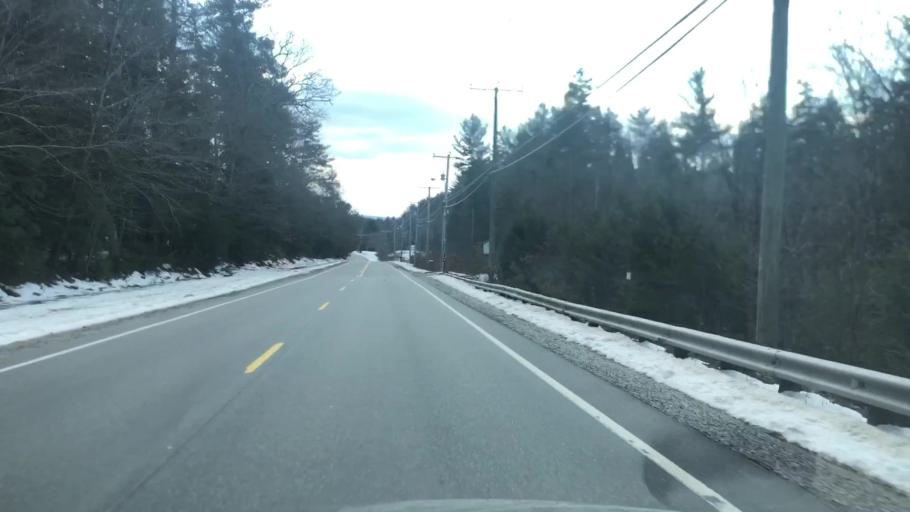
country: US
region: New Hampshire
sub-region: Hillsborough County
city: Mont Vernon
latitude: 42.8668
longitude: -71.6691
